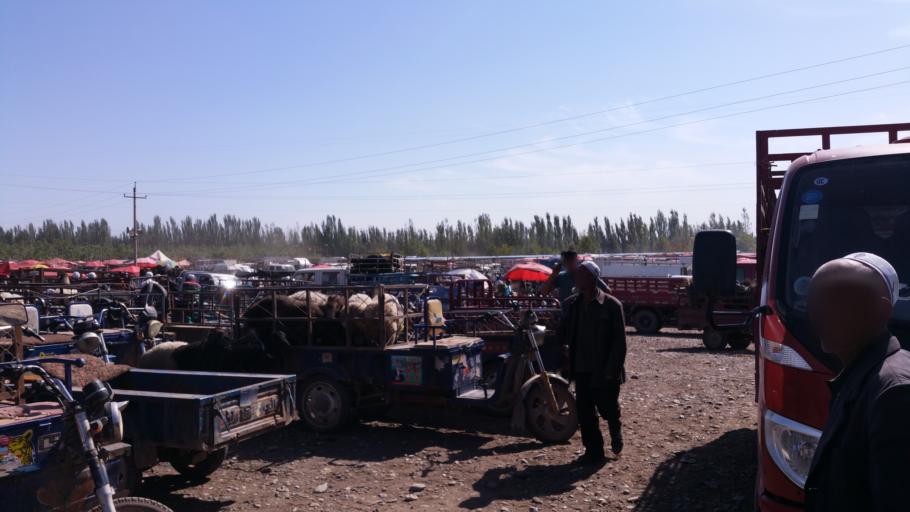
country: CN
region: Xinjiang Uygur Zizhiqu
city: Kashi
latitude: 39.5230
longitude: 75.9314
